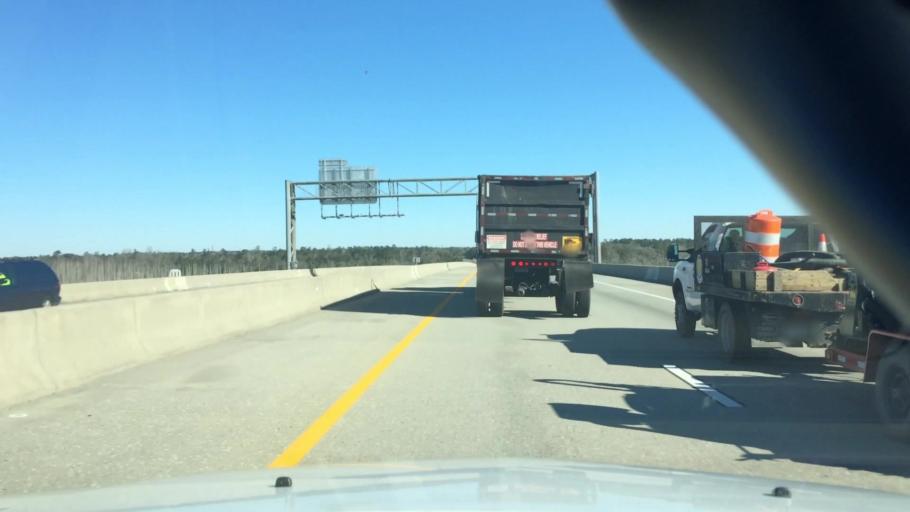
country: US
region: North Carolina
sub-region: New Hanover County
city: Wrightsboro
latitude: 34.3006
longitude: -77.9580
